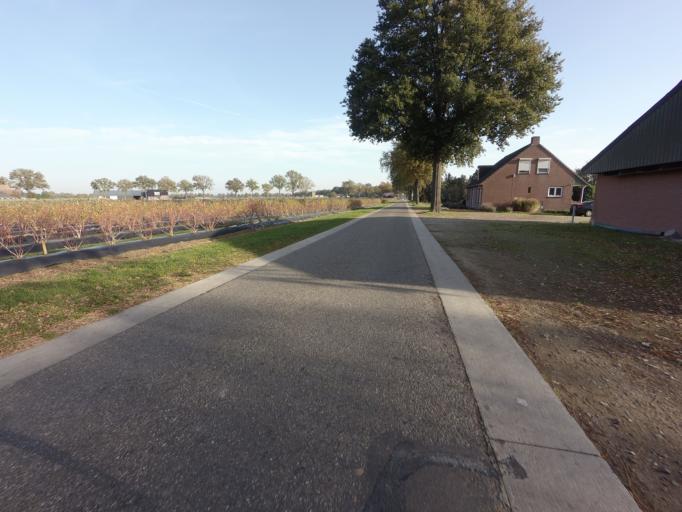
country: NL
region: Limburg
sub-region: Gemeente Roerdalen
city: Montfort
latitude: 51.1120
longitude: 5.9546
